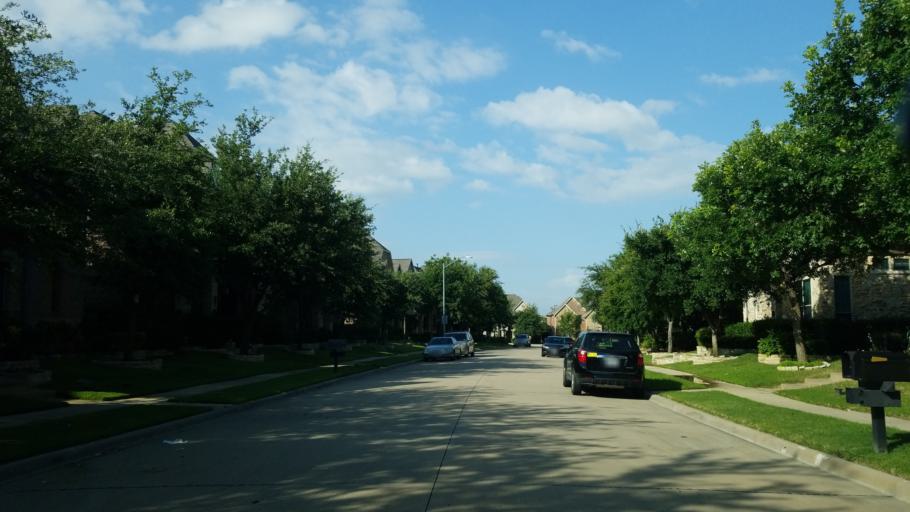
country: US
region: Texas
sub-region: Dallas County
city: Coppell
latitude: 32.9235
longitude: -96.9715
